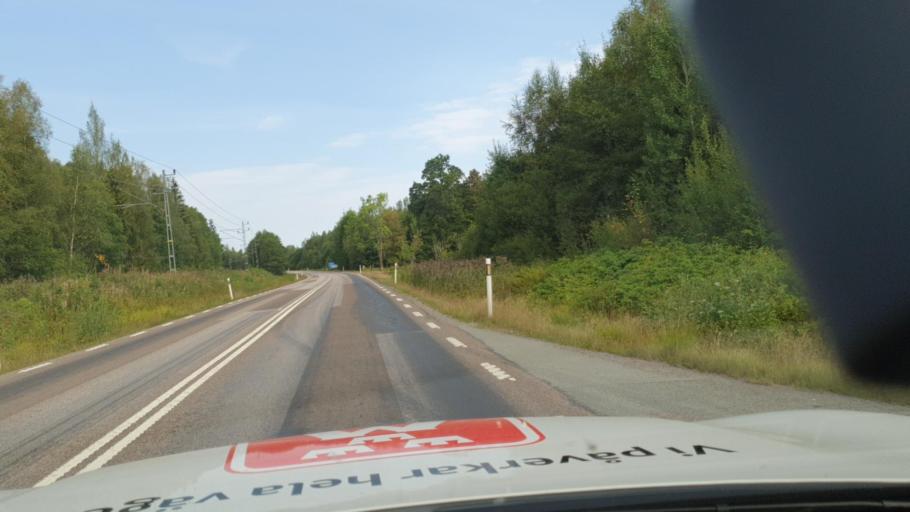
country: SE
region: Vaestra Goetaland
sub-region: Melleruds Kommun
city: Mellerud
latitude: 58.7345
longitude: 12.3553
